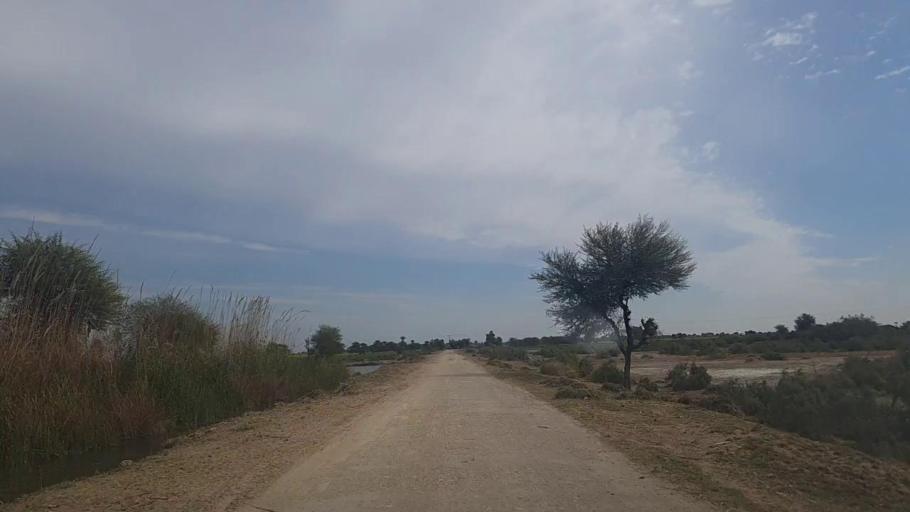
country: PK
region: Sindh
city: Sinjhoro
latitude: 26.1337
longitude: 68.8341
